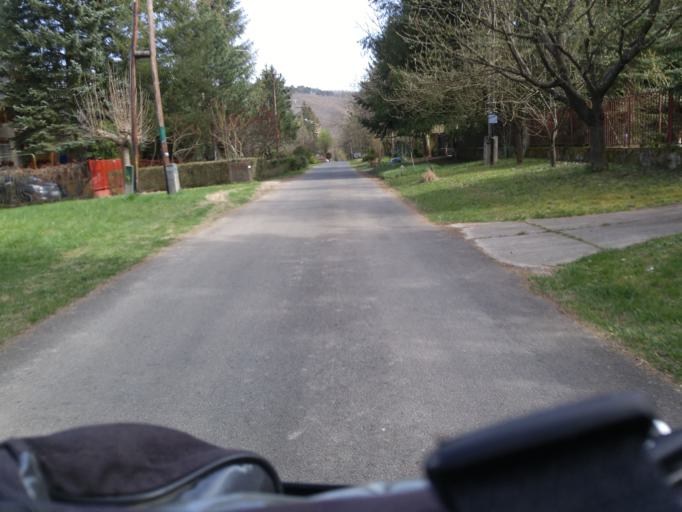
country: HU
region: Nograd
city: Retsag
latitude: 47.9200
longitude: 19.1753
